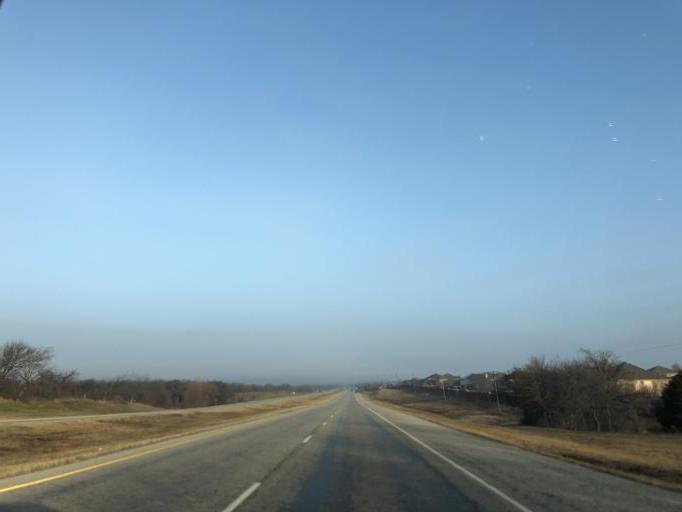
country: US
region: Texas
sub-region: Dallas County
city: Cedar Hill
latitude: 32.6442
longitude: -96.9738
